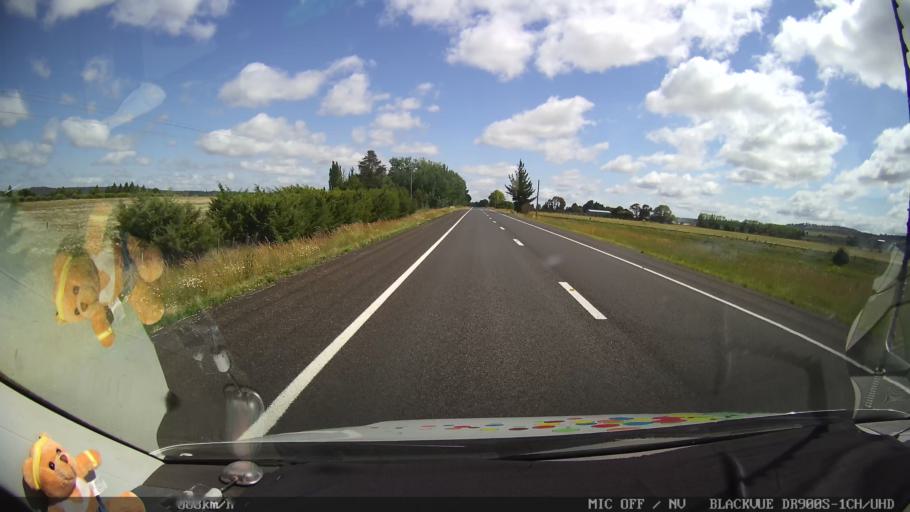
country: AU
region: New South Wales
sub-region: Glen Innes Severn
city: Glen Innes
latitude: -29.8236
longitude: 151.7394
